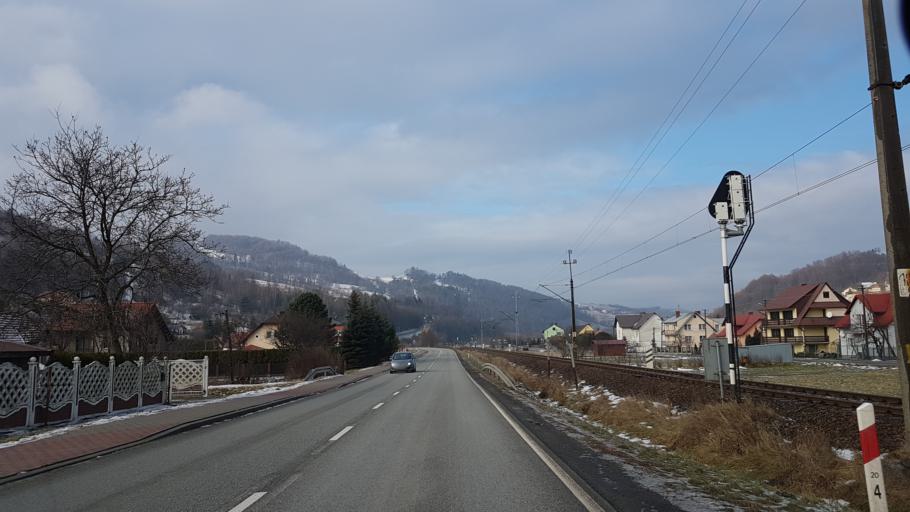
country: PL
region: Lesser Poland Voivodeship
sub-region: Powiat nowosadecki
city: Rytro
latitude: 49.4701
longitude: 20.6930
